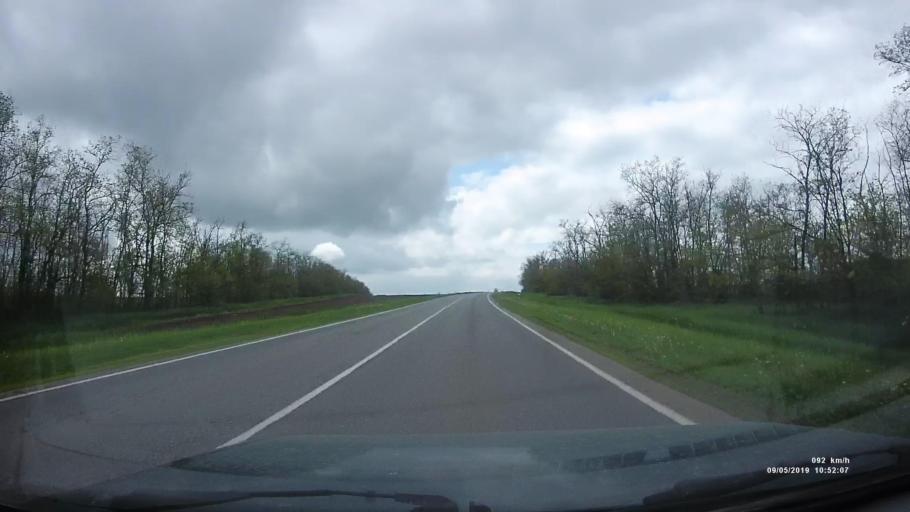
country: RU
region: Rostov
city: Peshkovo
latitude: 46.9050
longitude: 39.3548
